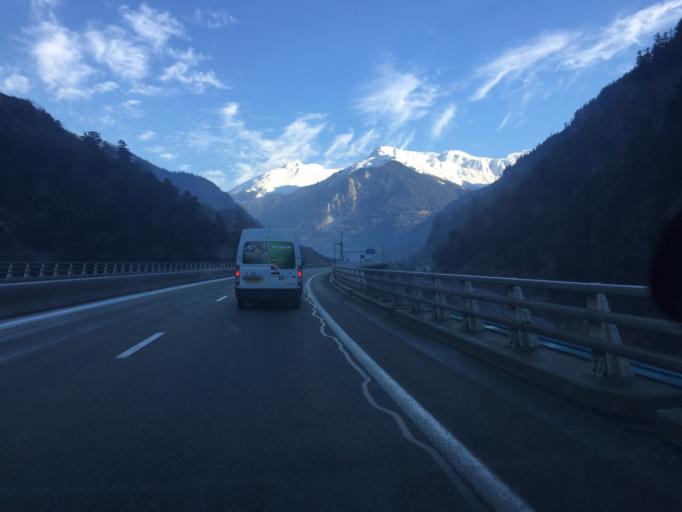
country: FR
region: Rhone-Alpes
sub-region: Departement de la Savoie
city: Modane
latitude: 45.1987
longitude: 6.6124
